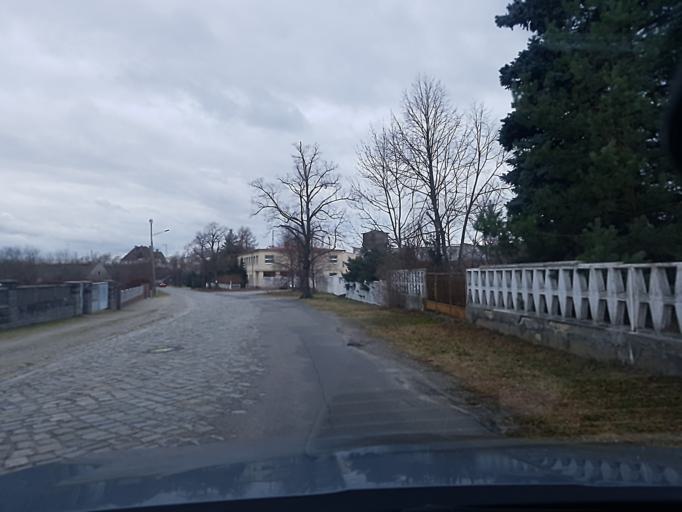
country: DE
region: Brandenburg
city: Doberlug-Kirchhain
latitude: 51.6227
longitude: 13.5676
